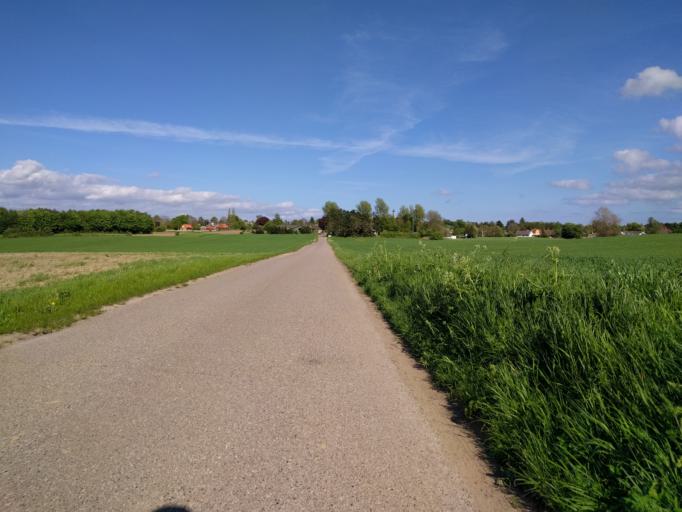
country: DK
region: Zealand
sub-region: Guldborgsund Kommune
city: Stubbekobing
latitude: 54.9257
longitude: 12.0395
